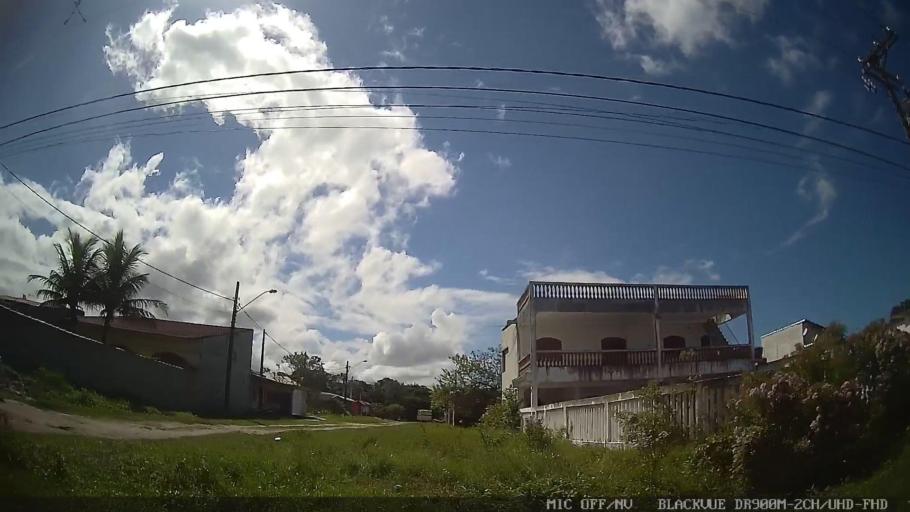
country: BR
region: Sao Paulo
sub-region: Itanhaem
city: Itanhaem
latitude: -24.2338
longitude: -46.8969
